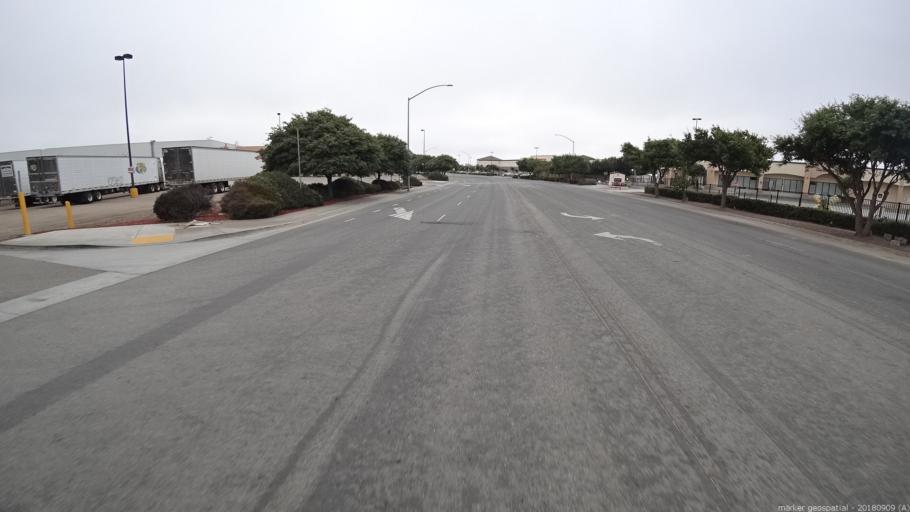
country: US
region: California
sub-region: Monterey County
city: Boronda
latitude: 36.7056
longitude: -121.6704
